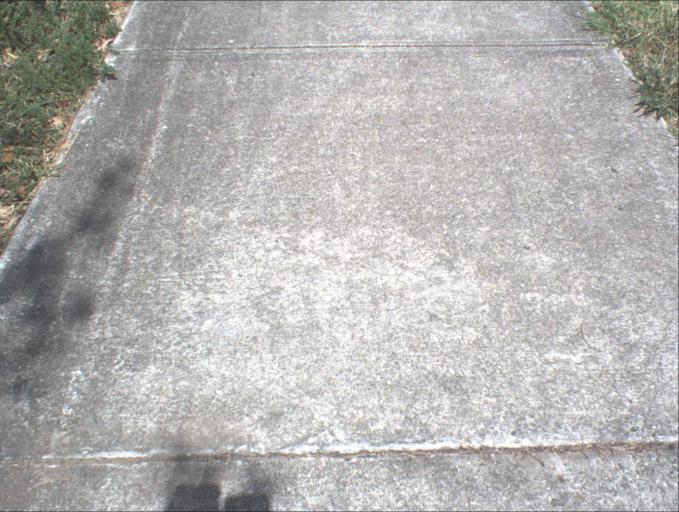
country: AU
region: Queensland
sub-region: Logan
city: Woodridge
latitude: -27.6164
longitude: 153.1023
